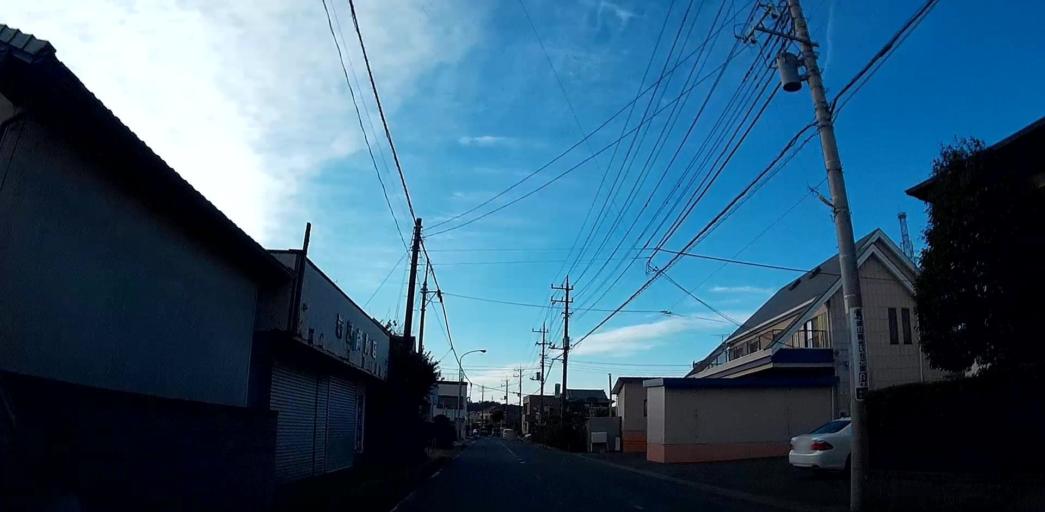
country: JP
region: Chiba
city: Omigawa
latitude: 35.8401
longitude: 140.6636
